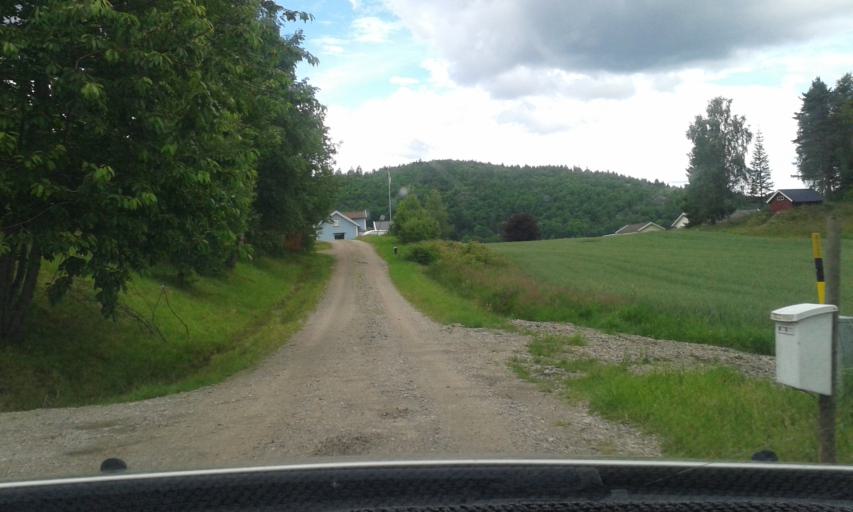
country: SE
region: Vaestra Goetaland
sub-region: Lilla Edets Kommun
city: Lilla Edet
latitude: 58.1397
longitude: 12.0886
